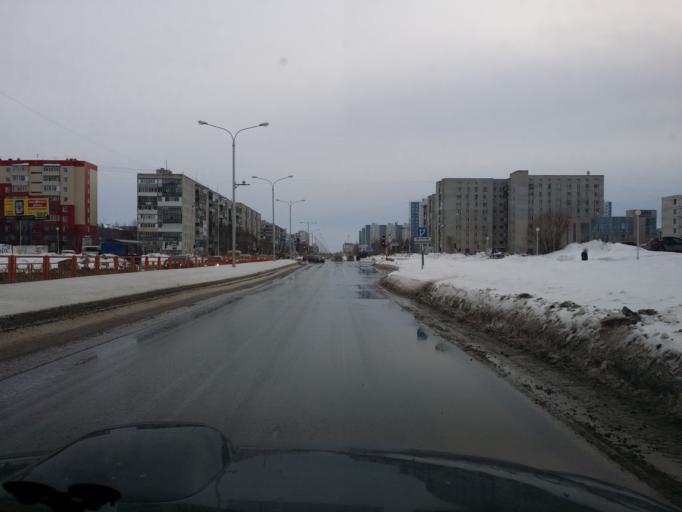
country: RU
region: Khanty-Mansiyskiy Avtonomnyy Okrug
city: Nizhnevartovsk
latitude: 60.9461
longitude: 76.6026
